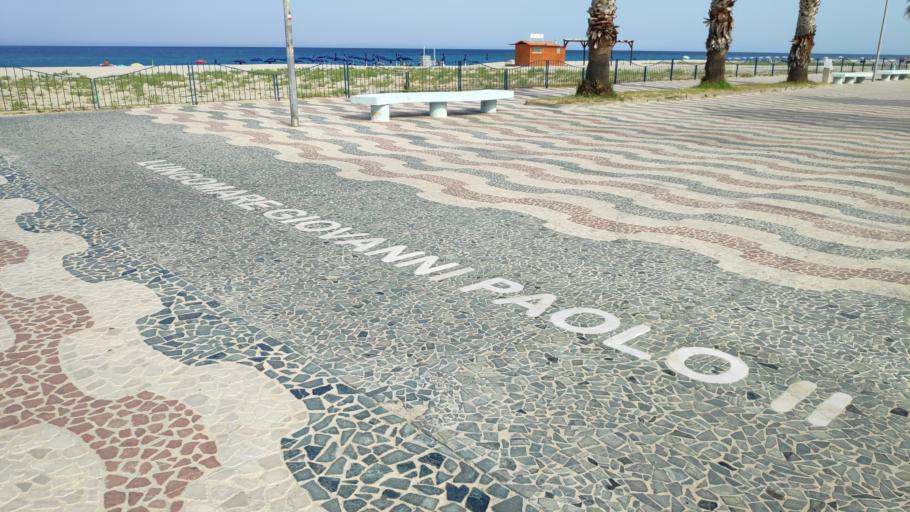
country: IT
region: Calabria
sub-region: Provincia di Catanzaro
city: Soverato Marina
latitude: 38.6877
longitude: 16.5555
